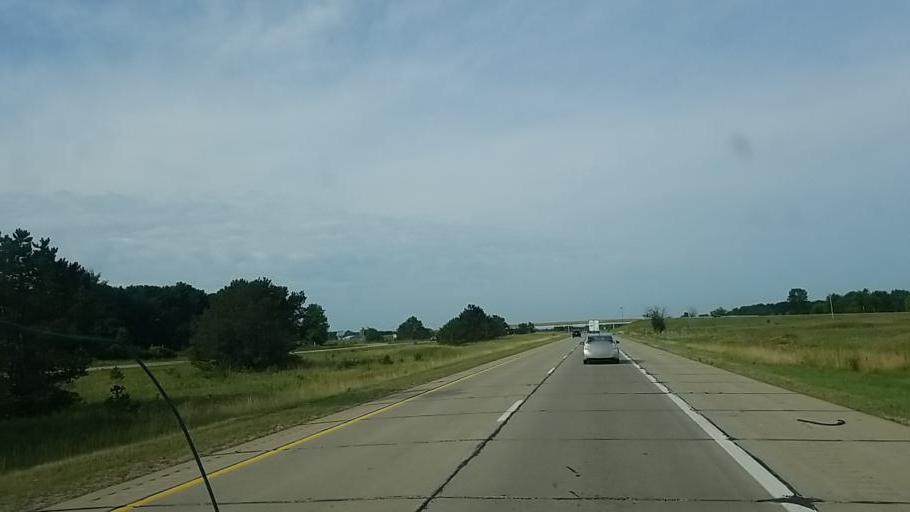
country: US
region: Michigan
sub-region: Eaton County
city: Charlotte
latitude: 42.5194
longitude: -84.8314
